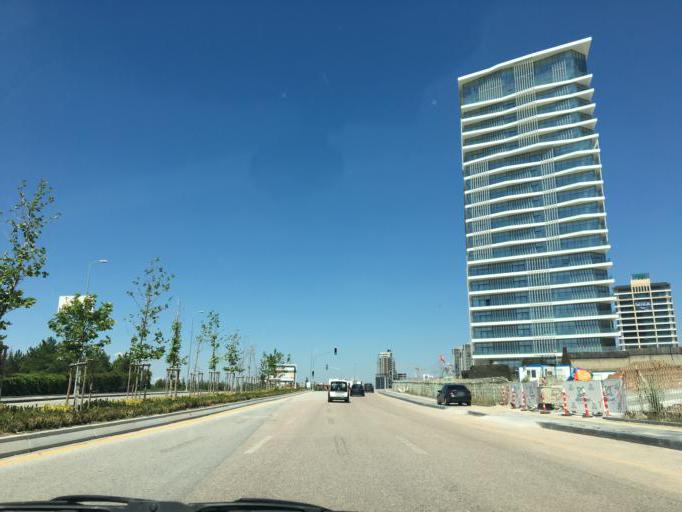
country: TR
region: Ankara
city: Batikent
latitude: 39.9120
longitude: 32.7759
